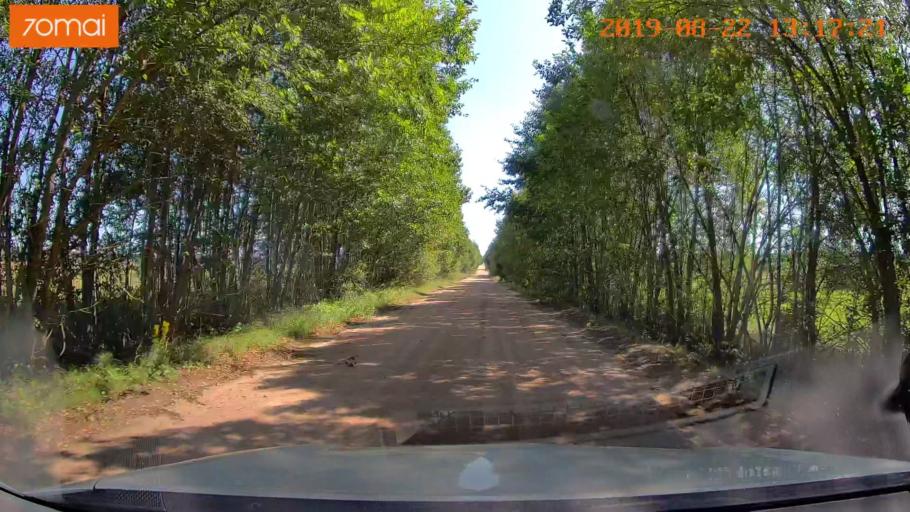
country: BY
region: Minsk
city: Prawdzinski
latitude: 53.2489
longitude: 27.9209
